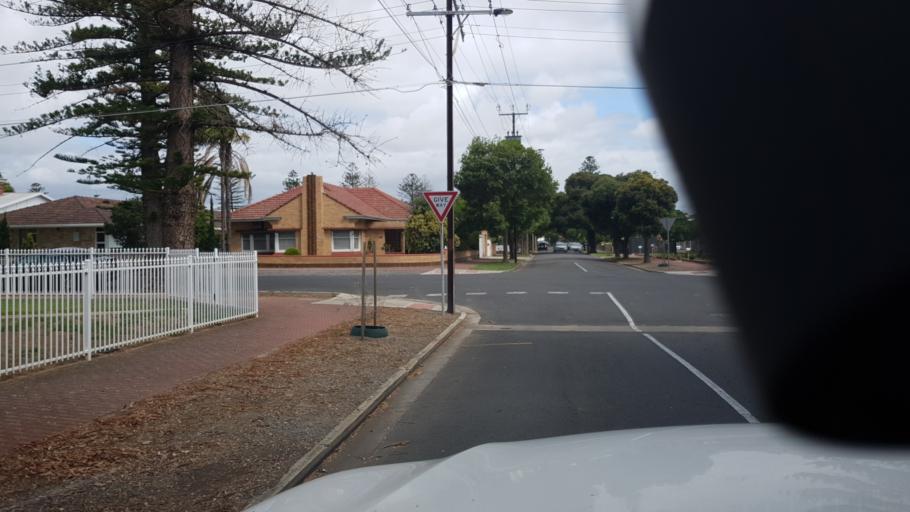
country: AU
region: South Australia
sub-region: Holdfast Bay
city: Glenelg East
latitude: -34.9775
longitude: 138.5269
